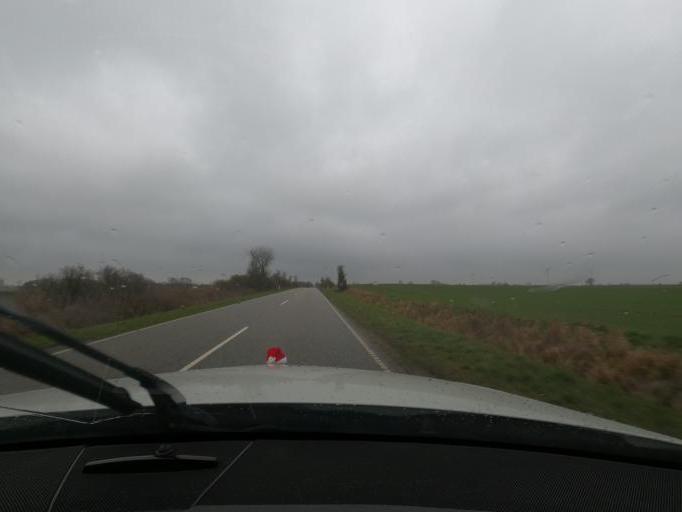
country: DK
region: South Denmark
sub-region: Haderslev Kommune
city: Starup
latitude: 55.2330
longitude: 9.6425
